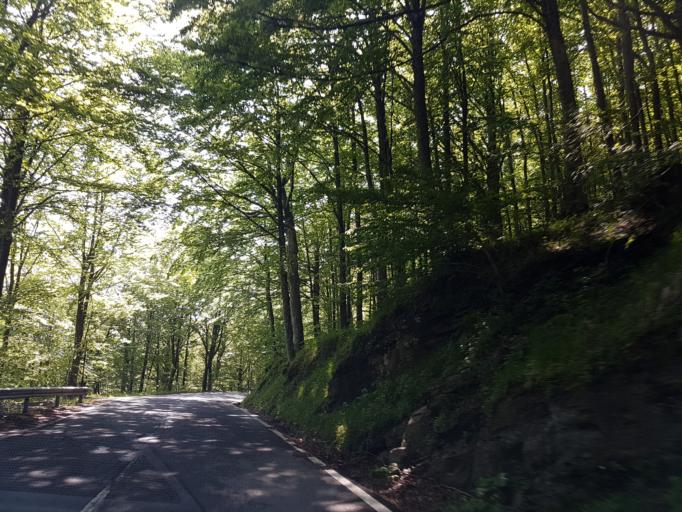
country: IT
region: Emilia-Romagna
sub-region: Forli-Cesena
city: San Piero in Bagno
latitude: 43.7983
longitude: 11.9082
